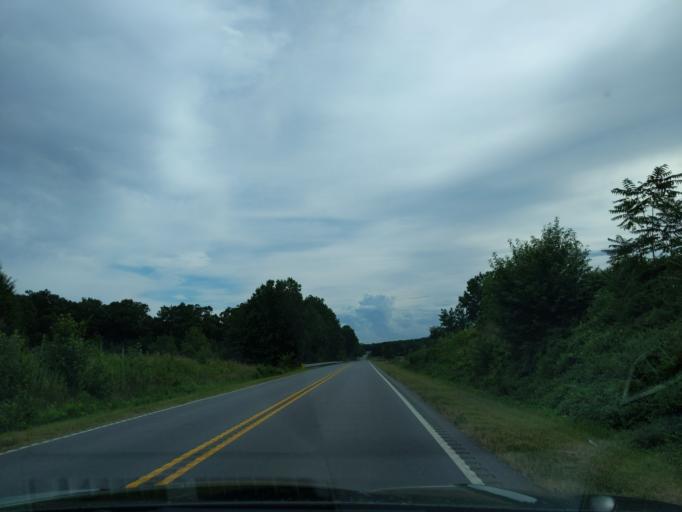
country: US
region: North Carolina
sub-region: Cabarrus County
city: Mount Pleasant
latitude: 35.4485
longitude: -80.3529
